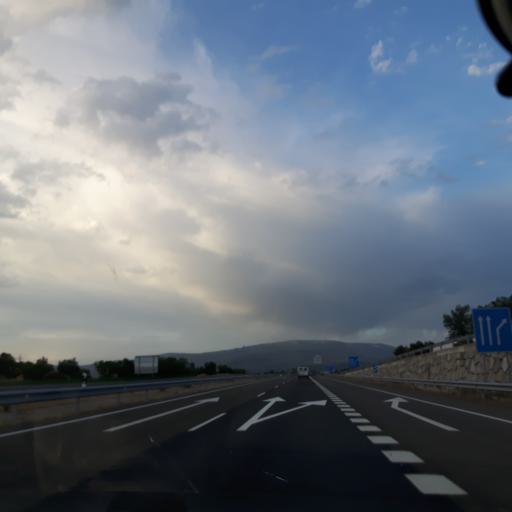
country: ES
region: Castille and Leon
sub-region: Provincia de Salamanca
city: Nava de Bejar
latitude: 40.4866
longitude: -5.6769
